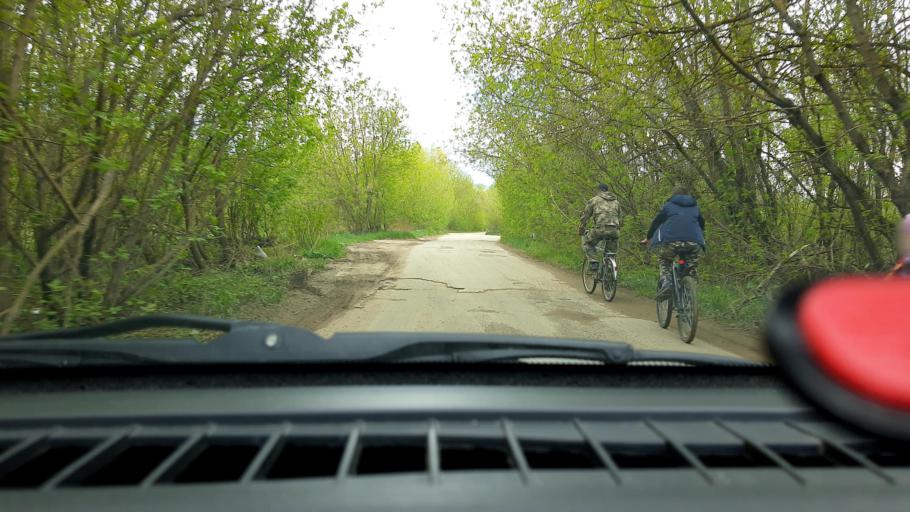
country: RU
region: Nizjnij Novgorod
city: Neklyudovo
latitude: 56.3874
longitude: 43.8413
